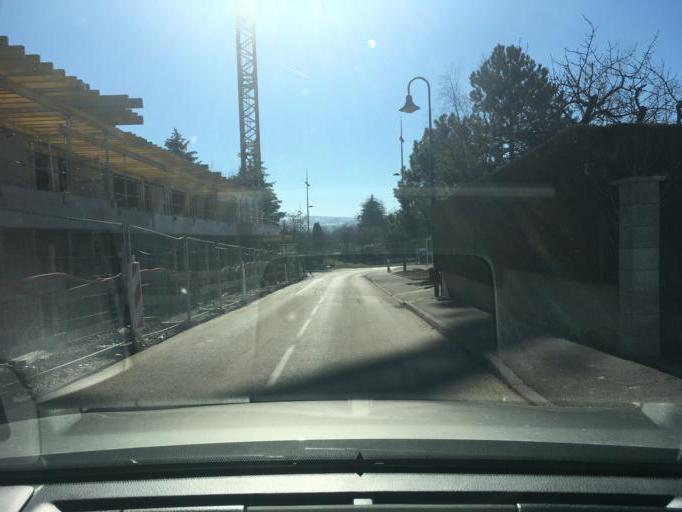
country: FR
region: Rhone-Alpes
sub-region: Departement de la Haute-Savoie
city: Vetraz-Monthoux
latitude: 46.1749
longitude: 6.2588
